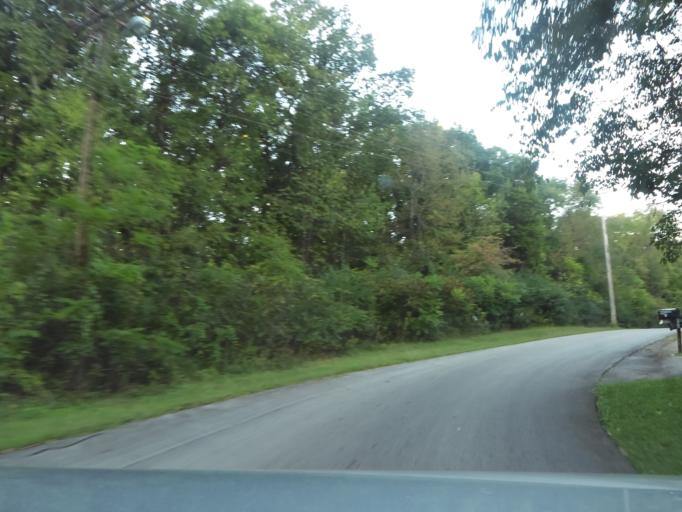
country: US
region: Tennessee
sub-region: Blount County
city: Alcoa
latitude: 35.7818
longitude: -83.9594
